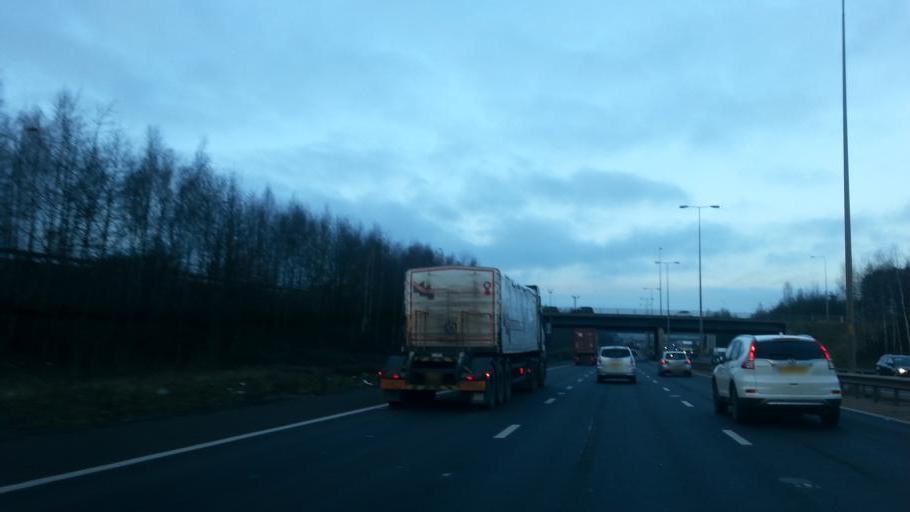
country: GB
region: England
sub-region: Worcestershire
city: Fernhill Heath
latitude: 52.2108
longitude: -2.1590
